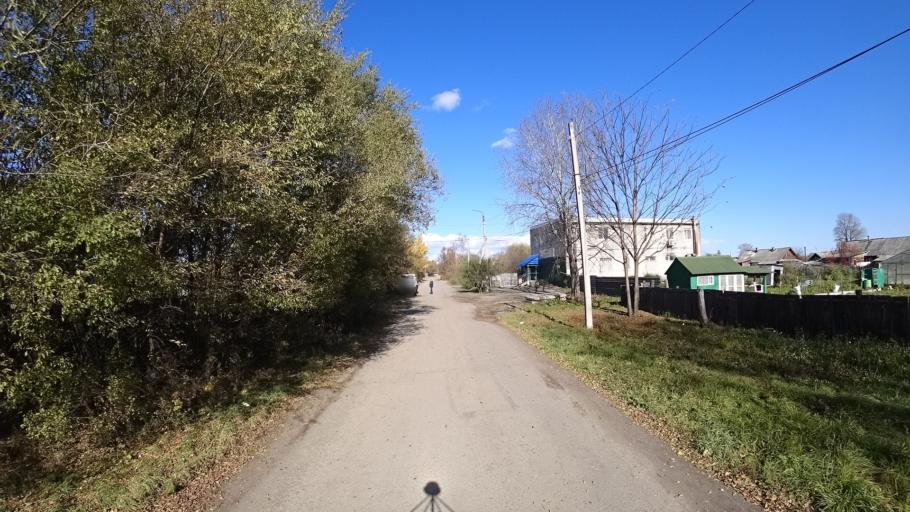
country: RU
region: Khabarovsk Krai
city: Amursk
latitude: 50.1002
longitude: 136.4971
